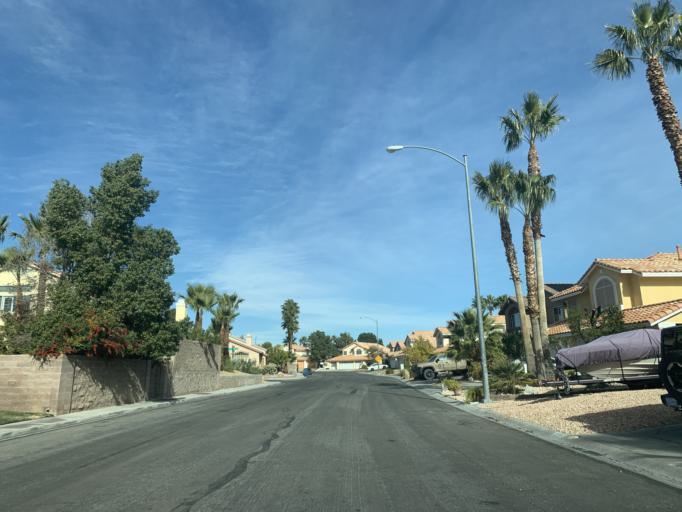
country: US
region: Nevada
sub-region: Clark County
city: Spring Valley
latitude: 36.1278
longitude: -115.2844
